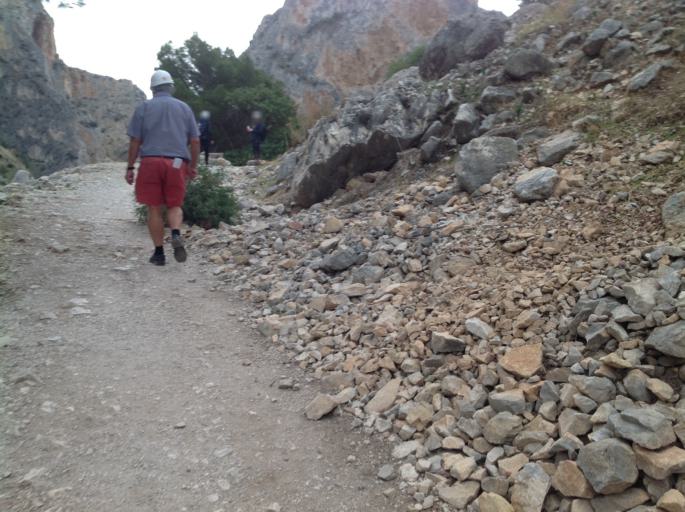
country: ES
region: Andalusia
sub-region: Provincia de Malaga
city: Carratraca
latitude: 36.9215
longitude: -4.7804
